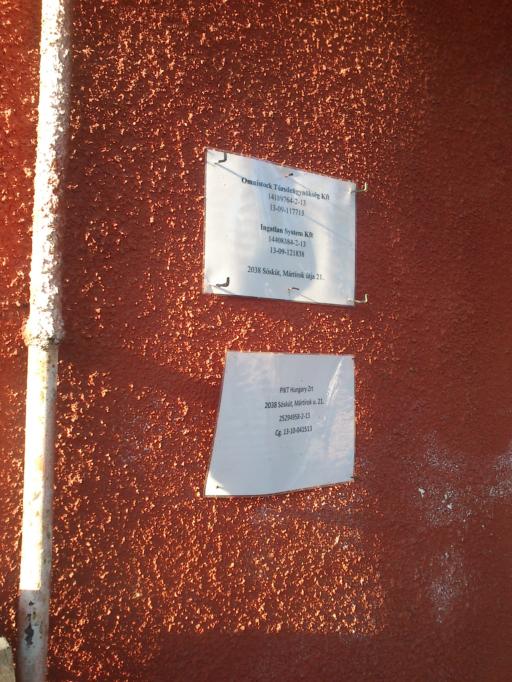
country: HU
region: Pest
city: Soskut
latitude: 47.4104
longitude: 18.8310
